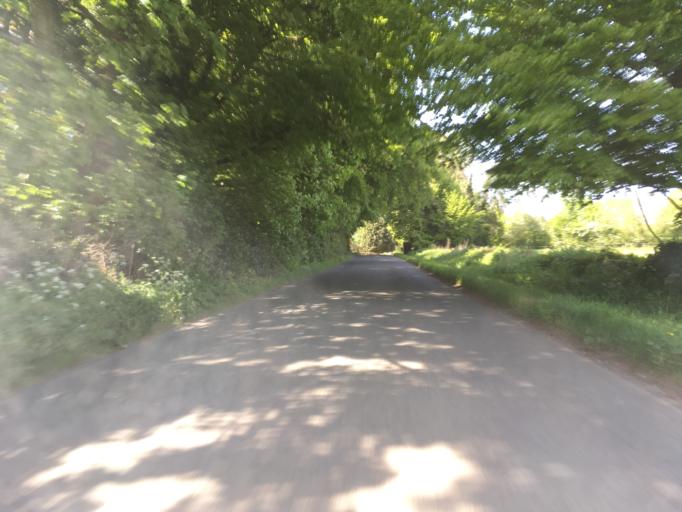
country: GB
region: England
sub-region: Gloucestershire
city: Coates
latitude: 51.6977
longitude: -2.0218
